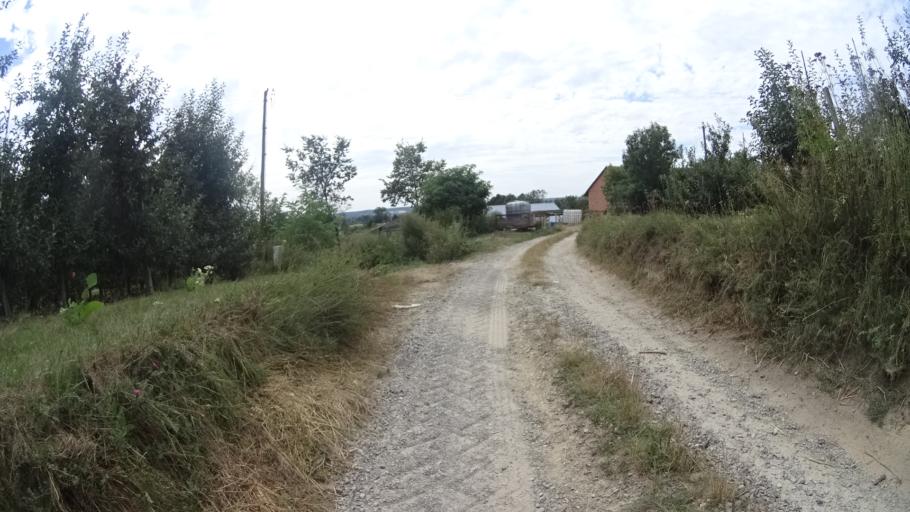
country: PL
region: Masovian Voivodeship
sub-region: Powiat bialobrzeski
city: Wysmierzyce
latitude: 51.6546
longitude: 20.8116
